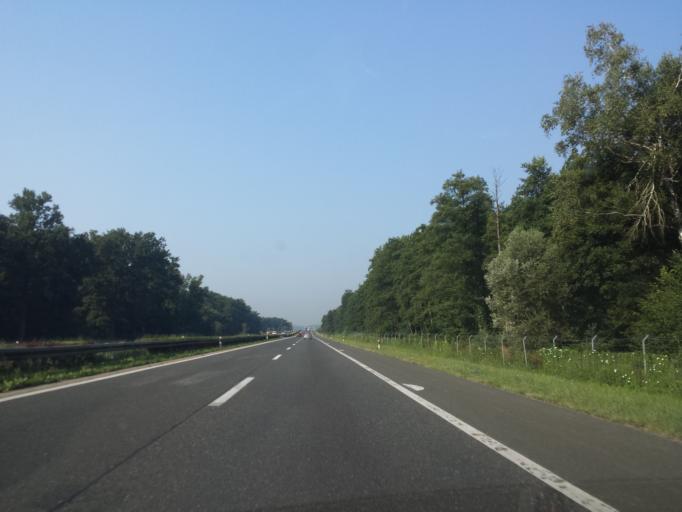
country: HR
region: Karlovacka
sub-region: Grad Karlovac
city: Karlovac
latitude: 45.5295
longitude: 15.5709
